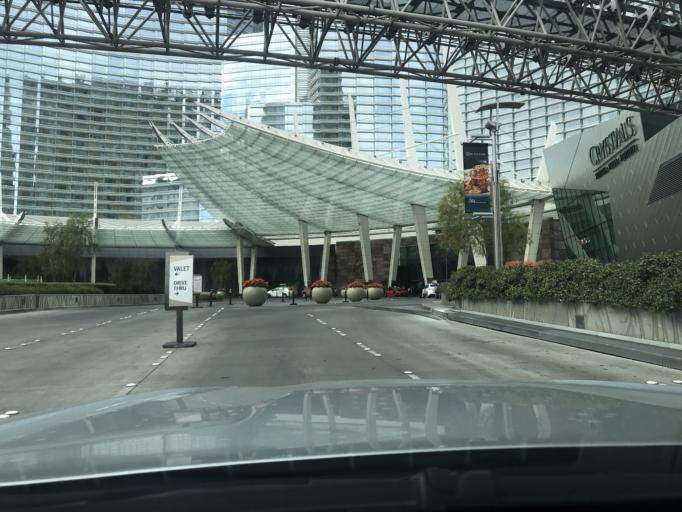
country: US
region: Nevada
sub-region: Clark County
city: Paradise
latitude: 36.1072
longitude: -115.1750
